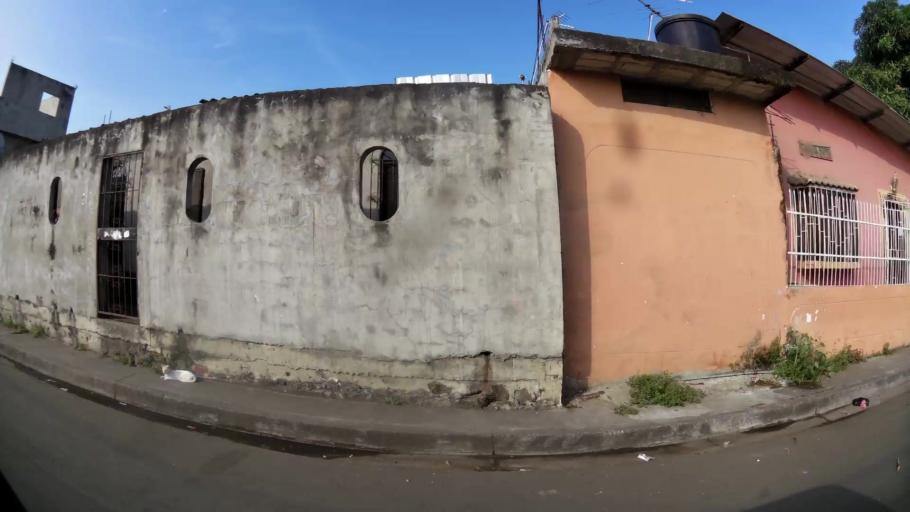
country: EC
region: Guayas
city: Eloy Alfaro
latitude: -2.1839
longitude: -79.8401
